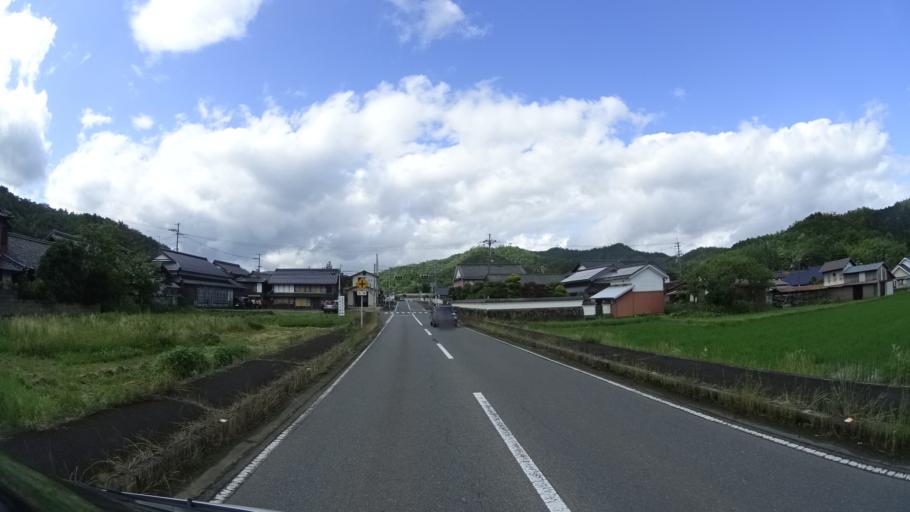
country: JP
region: Kyoto
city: Ayabe
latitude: 35.3672
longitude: 135.2397
